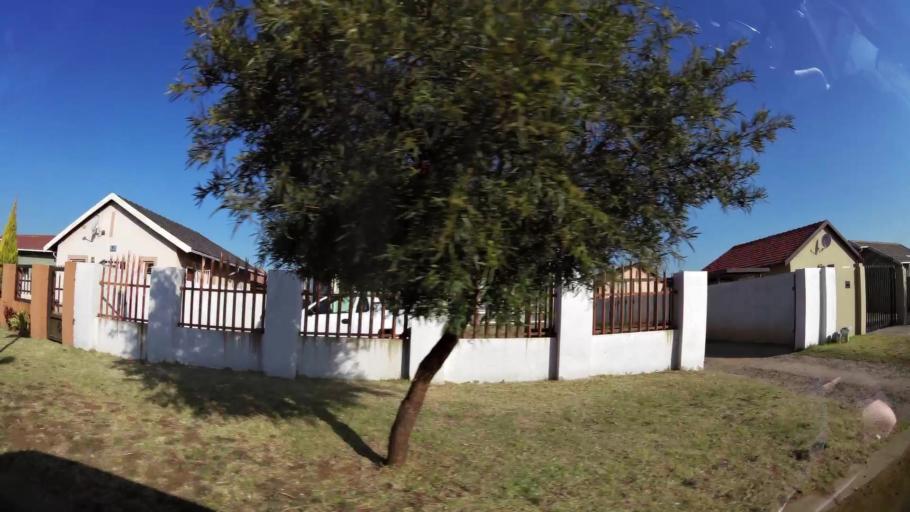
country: ZA
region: Gauteng
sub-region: West Rand District Municipality
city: Randfontein
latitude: -26.1891
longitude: 27.6977
